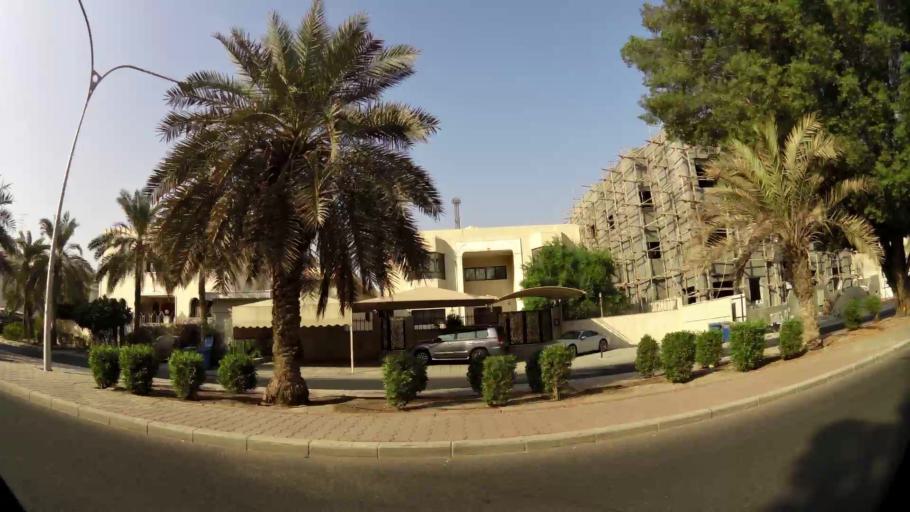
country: KW
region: Muhafazat Hawalli
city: Hawalli
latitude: 29.3202
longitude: 48.0395
